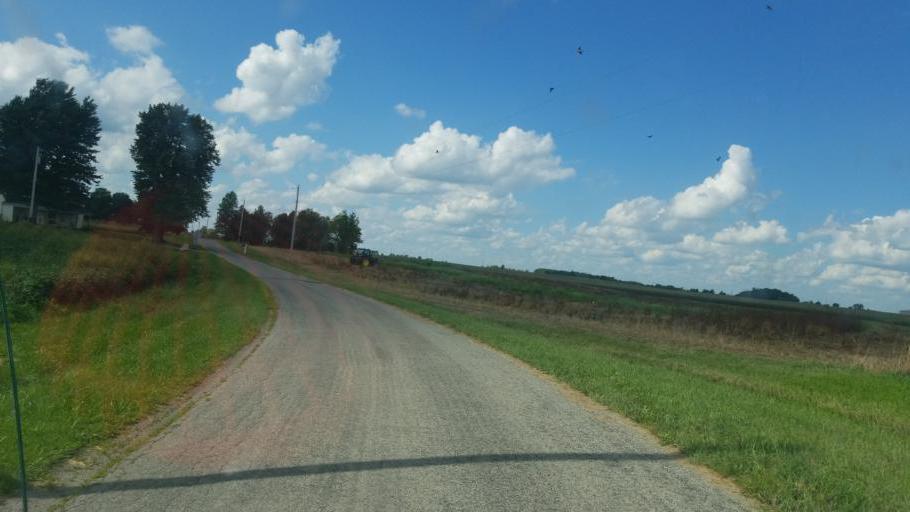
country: US
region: Ohio
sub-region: Union County
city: Richwood
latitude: 40.4903
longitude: -83.3508
